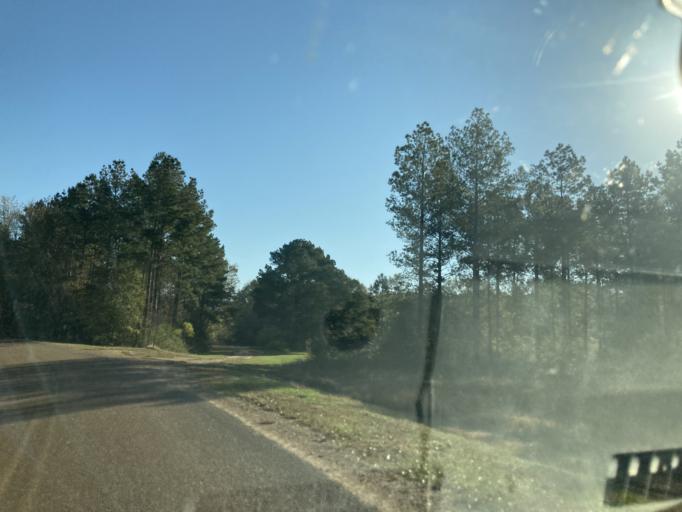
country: US
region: Mississippi
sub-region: Madison County
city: Canton
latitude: 32.7130
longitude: -90.1682
